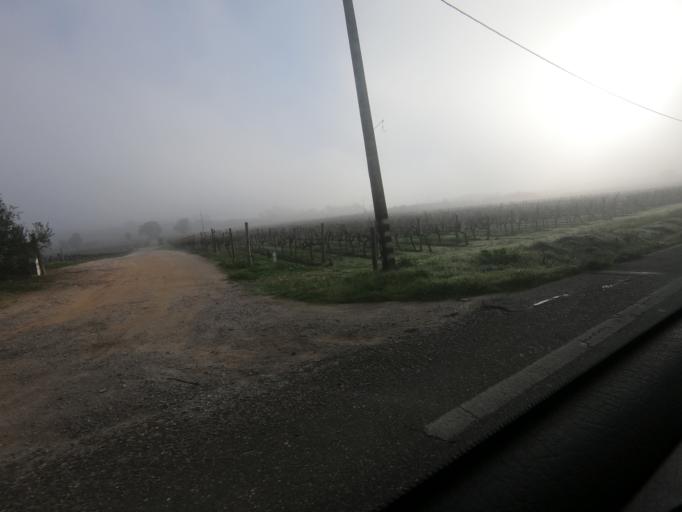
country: PT
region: Setubal
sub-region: Palmela
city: Pinhal Novo
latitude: 38.6086
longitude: -8.9085
